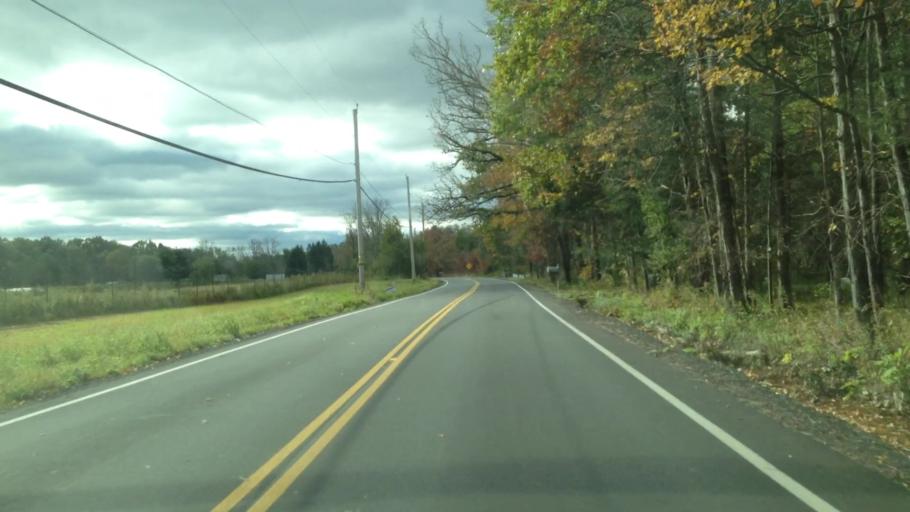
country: US
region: New York
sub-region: Ulster County
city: New Paltz
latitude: 41.7635
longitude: -74.0961
